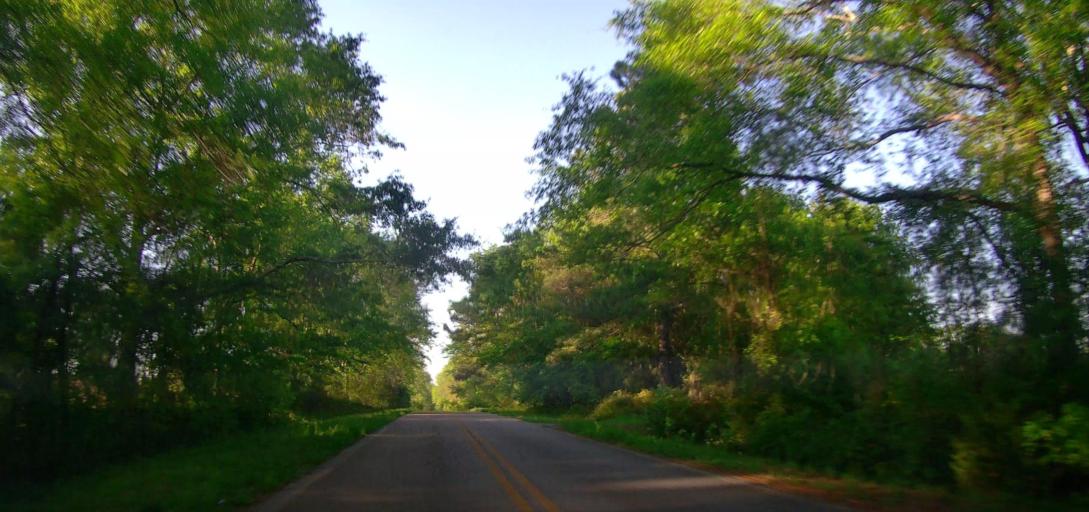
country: US
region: Georgia
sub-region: Macon County
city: Oglethorpe
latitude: 32.2833
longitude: -84.1467
